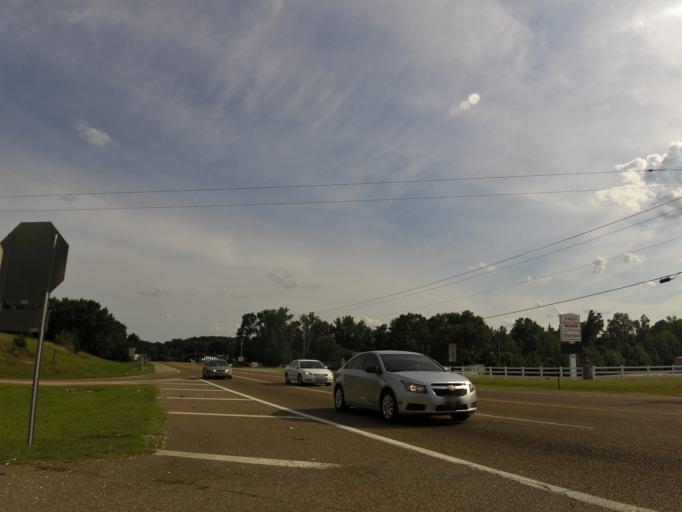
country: US
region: Tennessee
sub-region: Benton County
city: Camden
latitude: 36.0348
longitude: -88.1165
